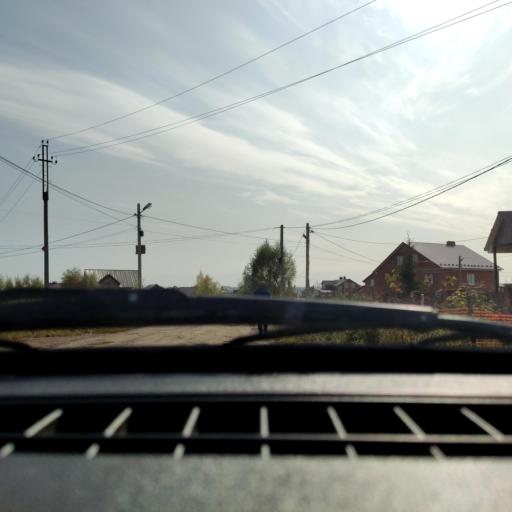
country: RU
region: Bashkortostan
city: Ufa
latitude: 54.6590
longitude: 56.0730
